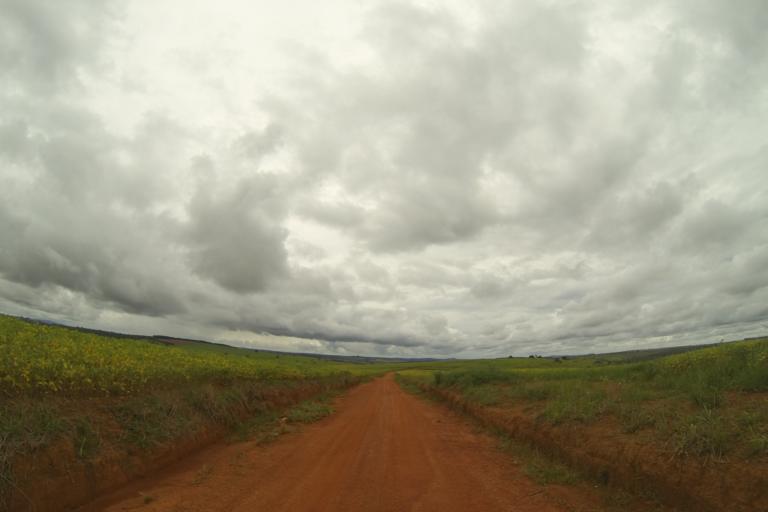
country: BR
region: Minas Gerais
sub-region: Ibia
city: Ibia
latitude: -19.7298
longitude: -46.5612
